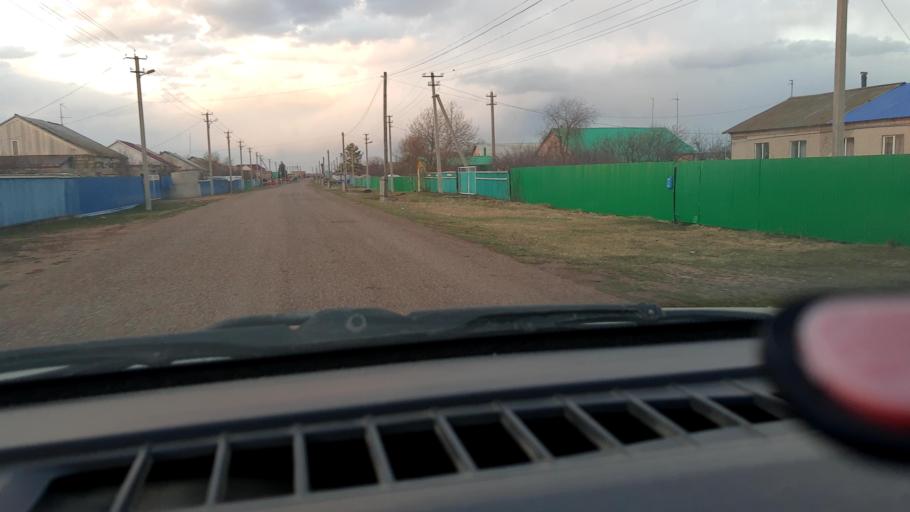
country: RU
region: Bashkortostan
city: Asanovo
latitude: 54.9059
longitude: 55.4861
